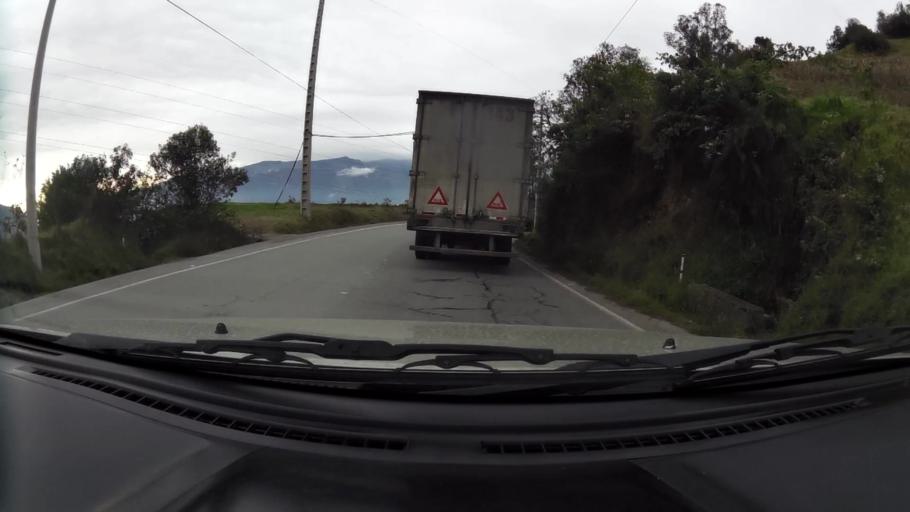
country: EC
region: Chimborazo
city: Alausi
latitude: -2.3078
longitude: -78.9285
